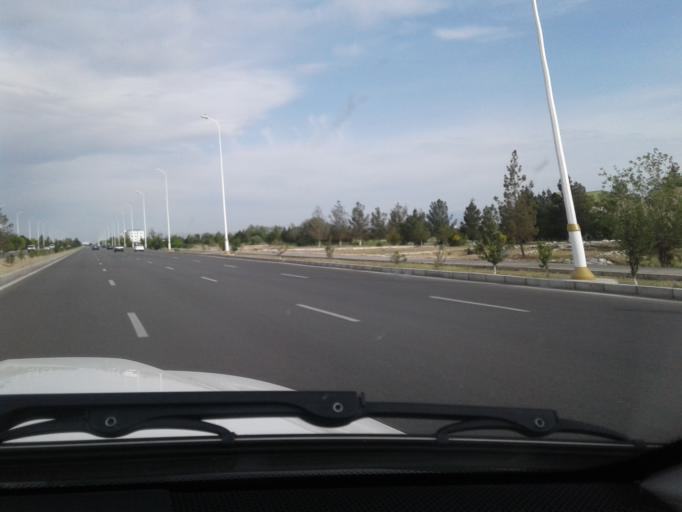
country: TM
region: Ahal
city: Ashgabat
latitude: 37.9980
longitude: 58.3043
